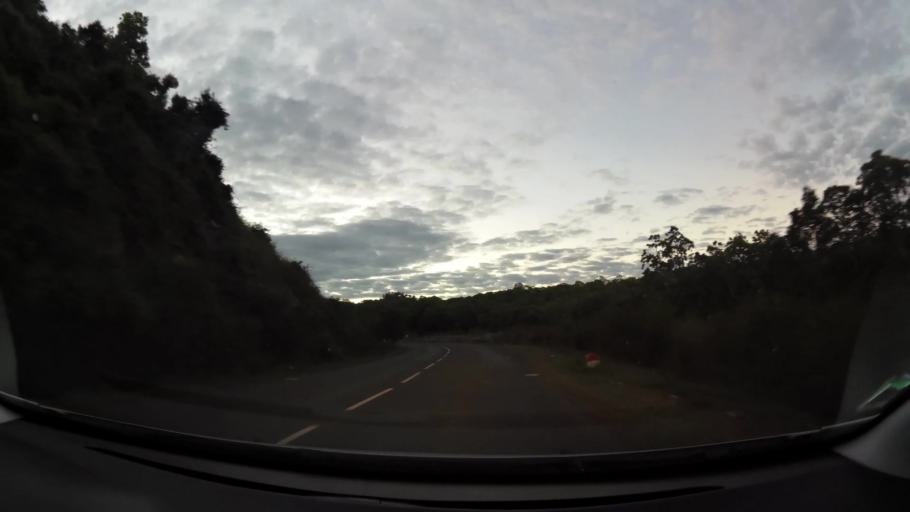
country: YT
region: Bandraboua
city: Bandraboua
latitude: -12.7280
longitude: 45.1297
